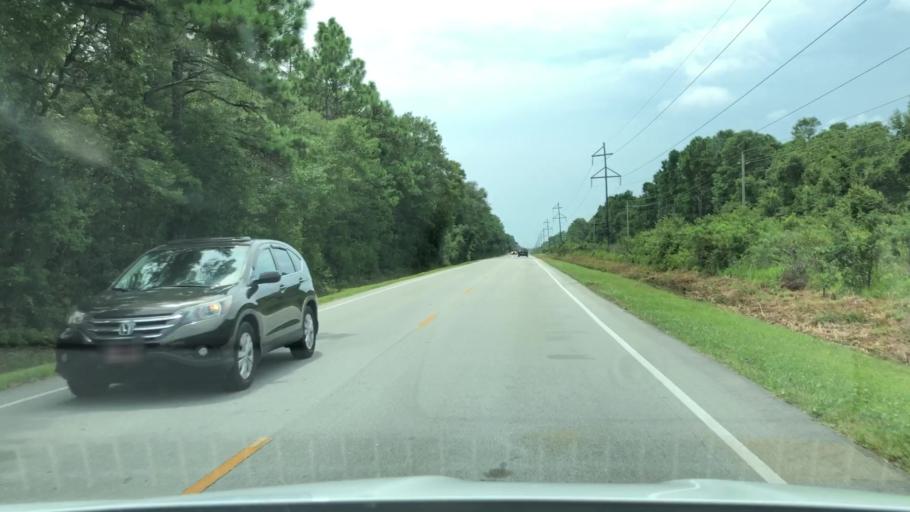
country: US
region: North Carolina
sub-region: Carteret County
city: Newport
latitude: 34.7583
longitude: -76.8728
